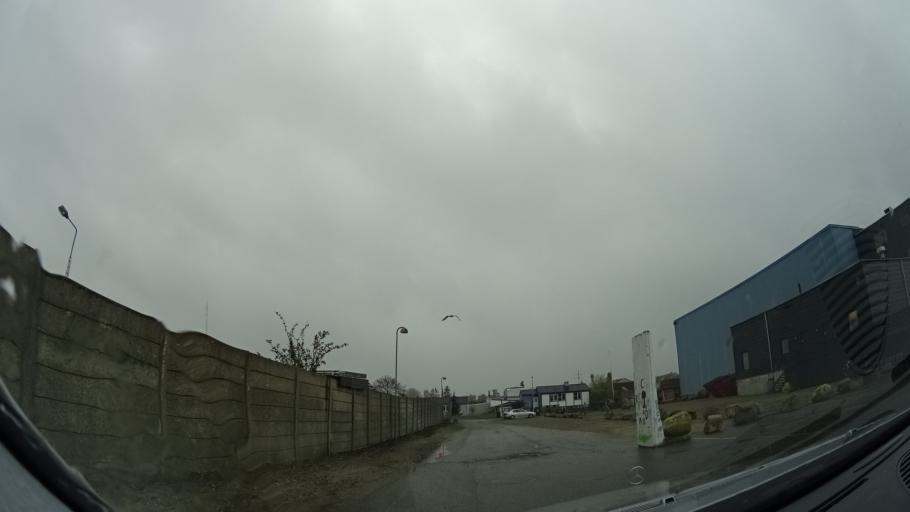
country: DK
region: Zealand
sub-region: Holbaek Kommune
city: Holbaek
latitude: 55.7199
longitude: 11.7229
